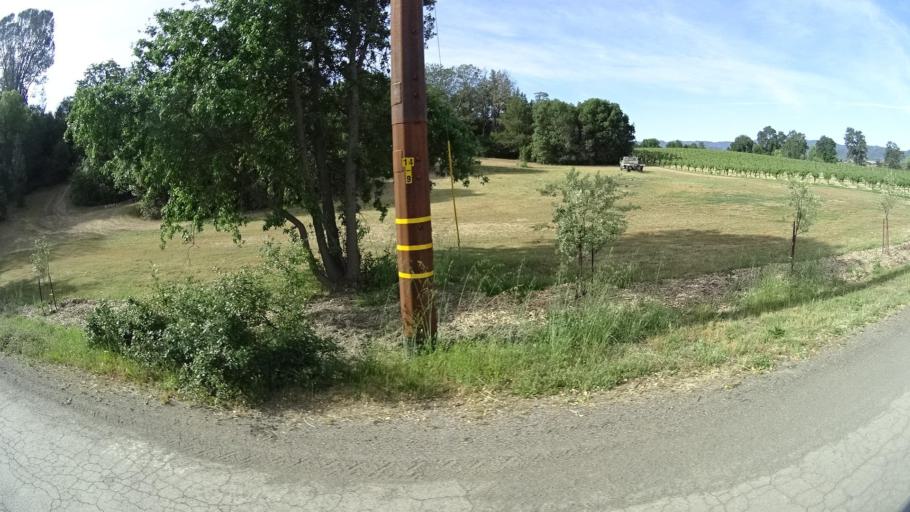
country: US
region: California
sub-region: Lake County
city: Kelseyville
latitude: 38.9827
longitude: -122.8614
